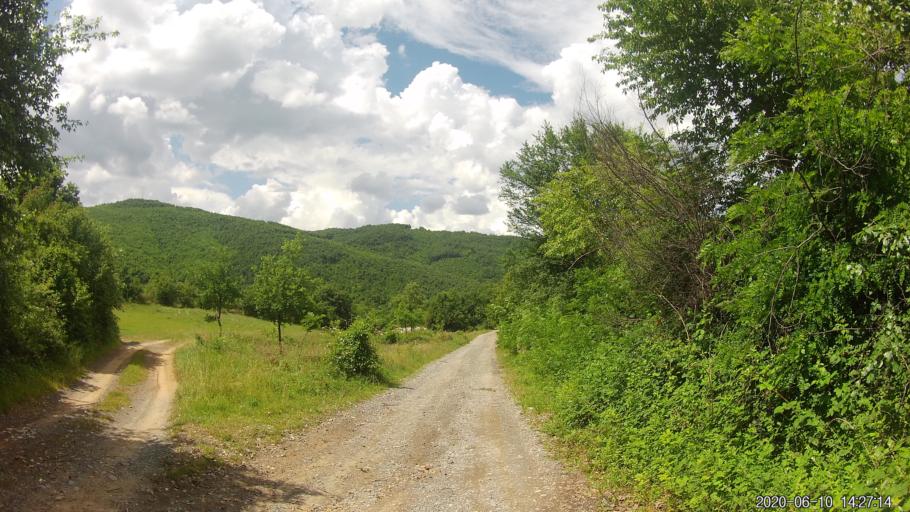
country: XK
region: Prizren
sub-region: Komuna e Therandes
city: Budakovo
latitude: 42.4102
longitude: 20.9148
